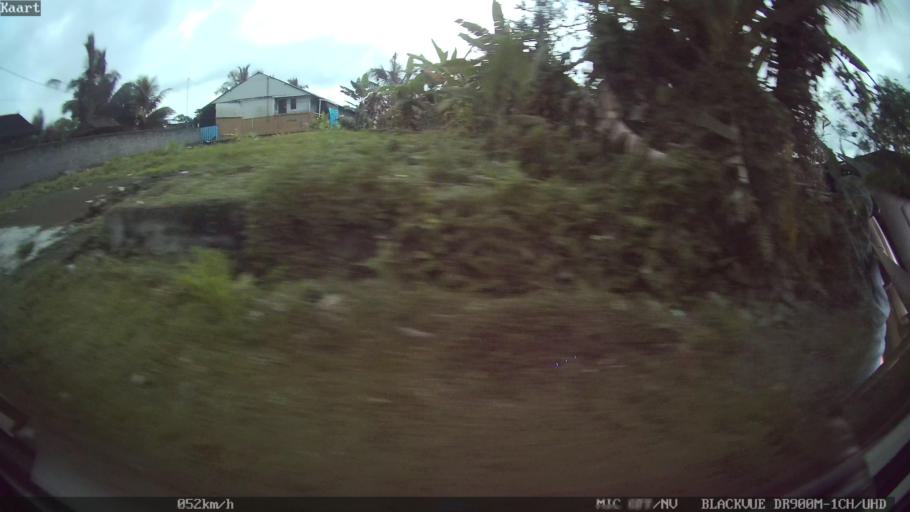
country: ID
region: Bali
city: Empalan
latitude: -8.4042
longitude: 115.1471
